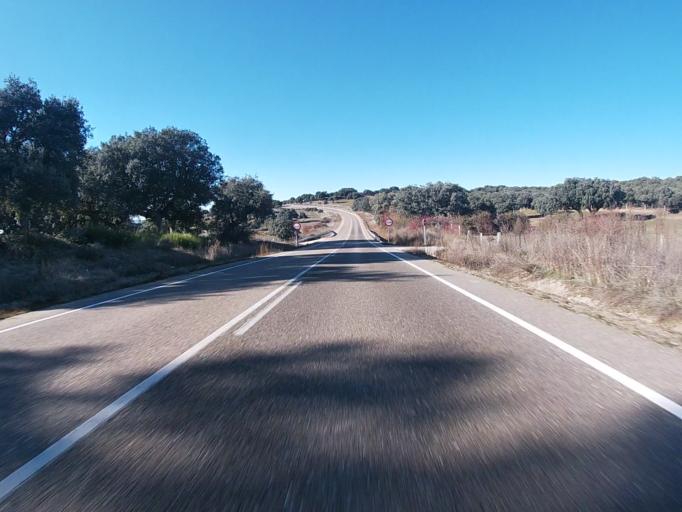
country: ES
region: Castille and Leon
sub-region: Provincia de Salamanca
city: Juzbado
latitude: 41.0774
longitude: -5.8437
